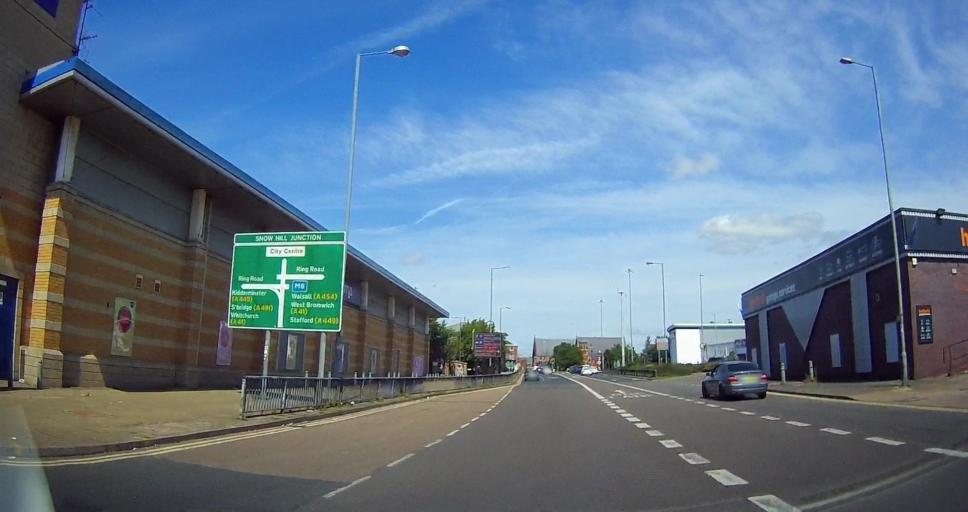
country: GB
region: England
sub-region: Wolverhampton
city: Wolverhampton
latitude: 52.5785
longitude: -2.1261
